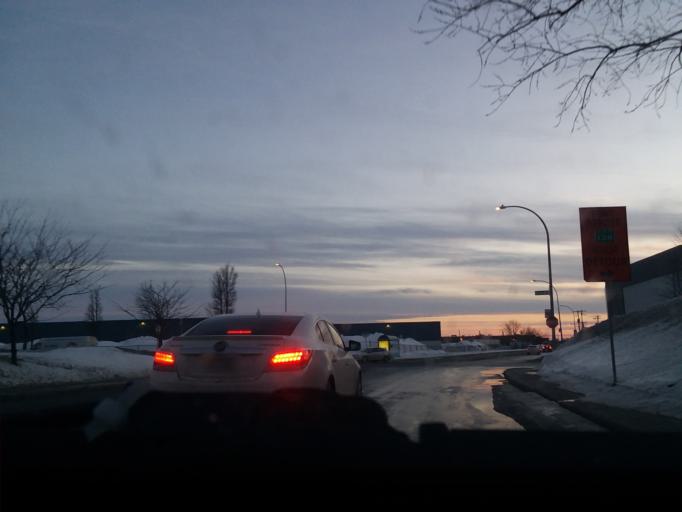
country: CA
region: Quebec
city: Saint-Raymond
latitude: 45.4476
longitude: -73.6208
